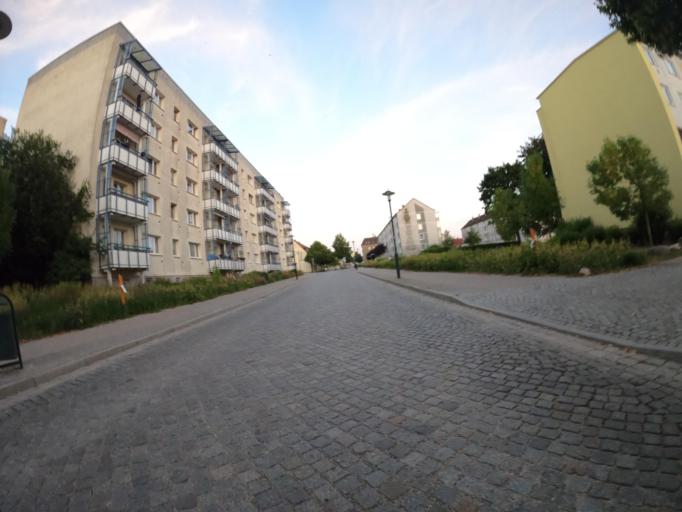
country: DE
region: Mecklenburg-Vorpommern
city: Woldegk
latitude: 53.4607
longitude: 13.5813
